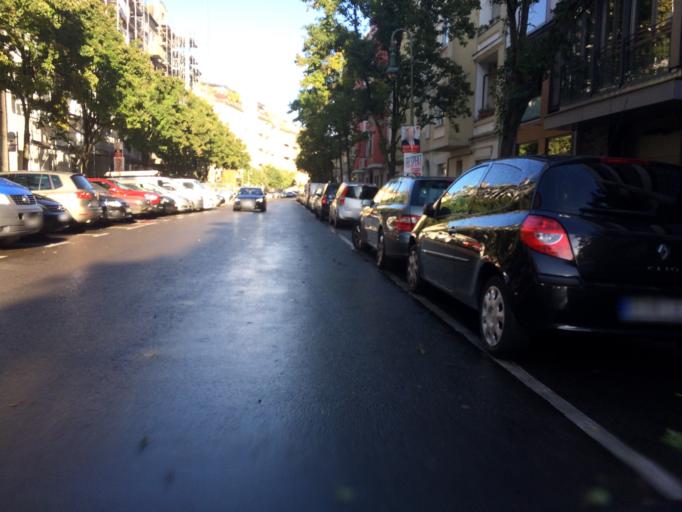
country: DE
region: Berlin
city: Gesundbrunnen
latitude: 52.5529
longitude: 13.4014
